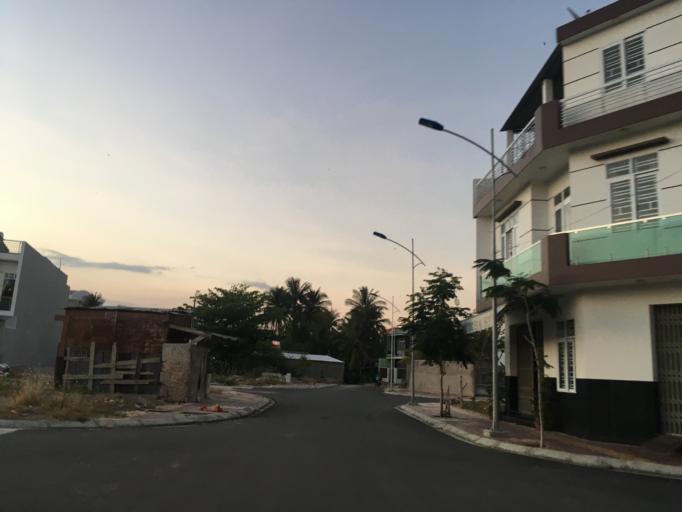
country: VN
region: Ninh Thuan
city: Phan Rang-Thap Cham
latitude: 11.5767
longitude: 108.9961
